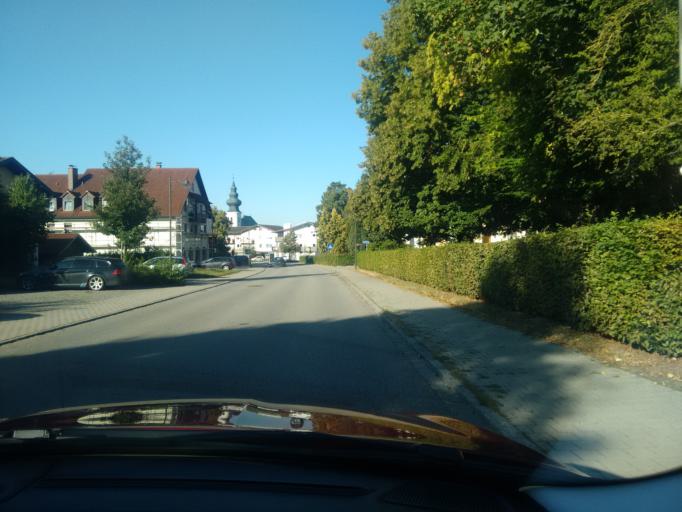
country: DE
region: Bavaria
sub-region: Upper Bavaria
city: Kirchweidach
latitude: 48.0874
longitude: 12.6452
